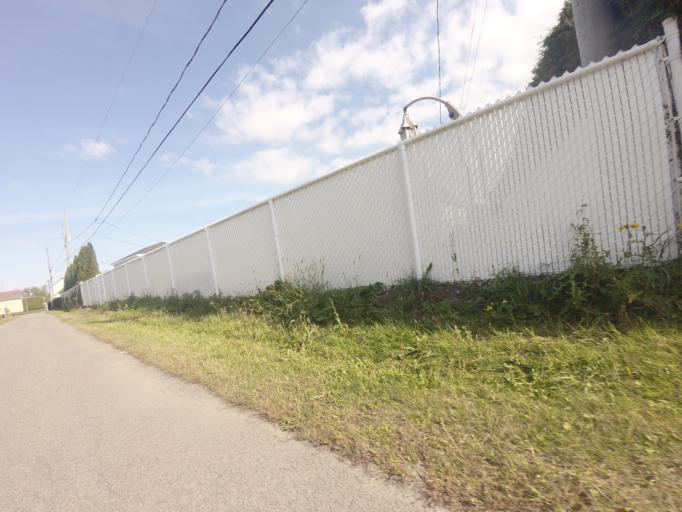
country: CA
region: Quebec
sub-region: Laurentides
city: Blainville
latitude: 45.7089
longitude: -73.9133
